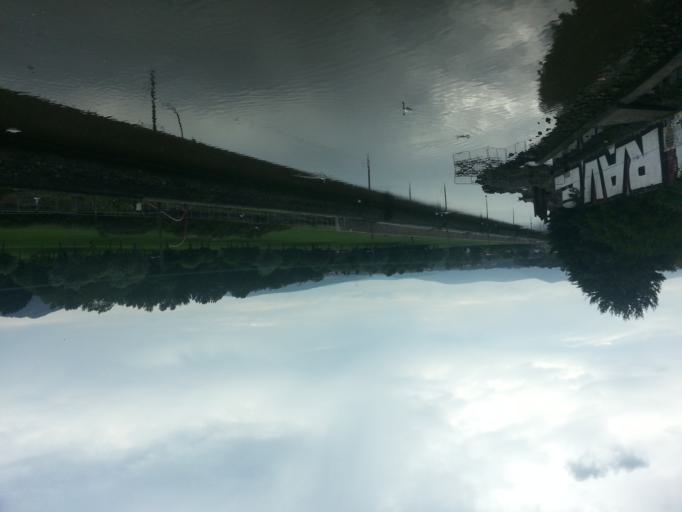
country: IE
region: Leinster
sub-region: Wicklow
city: Bray
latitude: 53.2085
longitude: -6.1031
